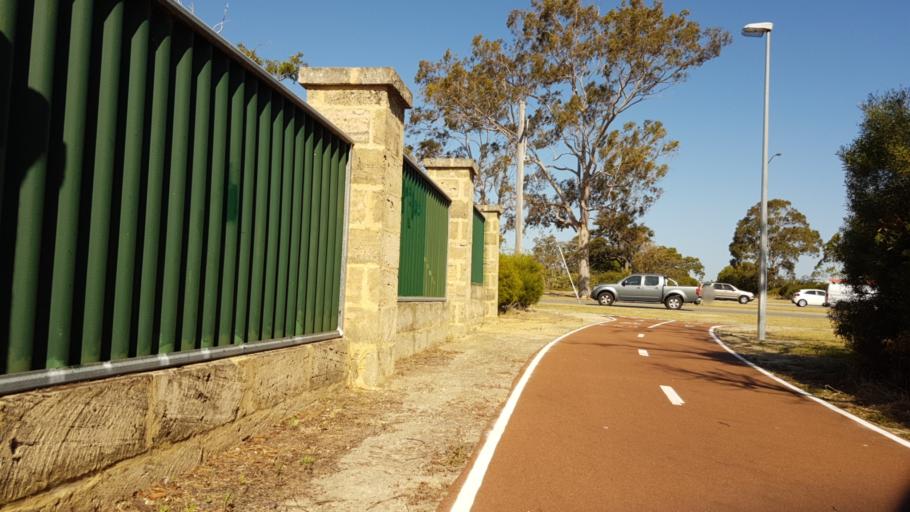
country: AU
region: Western Australia
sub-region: Stirling
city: Balcatta
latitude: -31.8565
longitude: 115.8124
